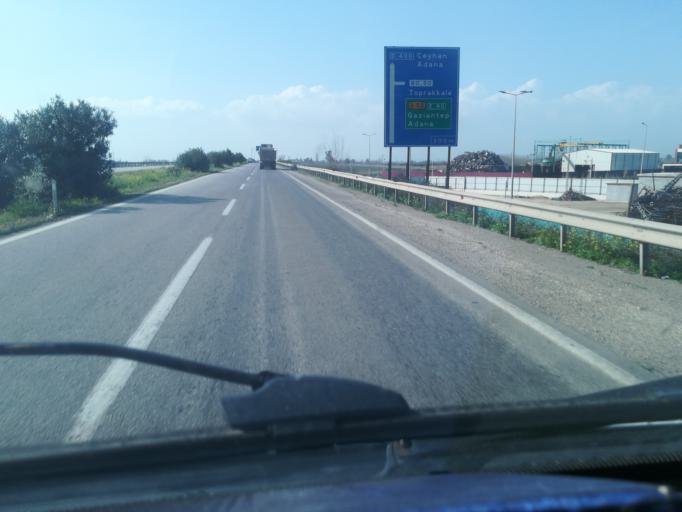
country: TR
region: Osmaniye
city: Toprakkale
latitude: 37.0718
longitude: 36.0896
